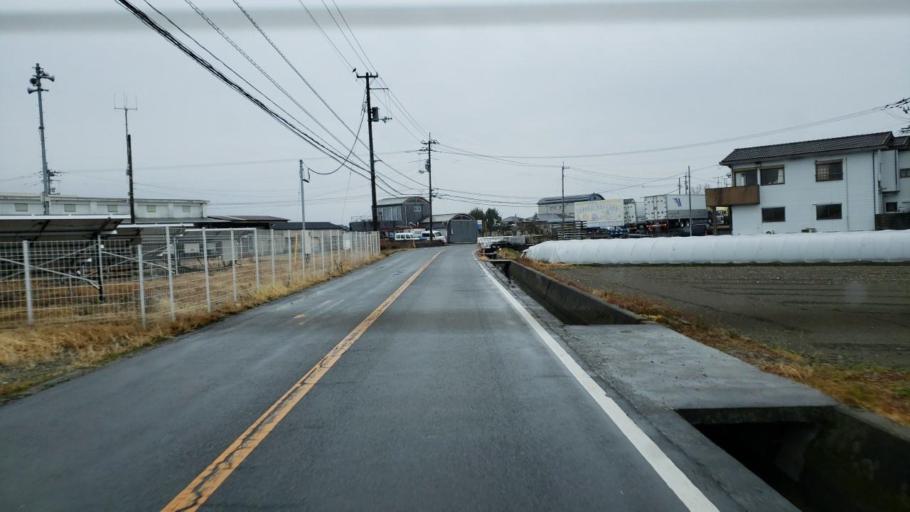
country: JP
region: Tokushima
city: Ishii
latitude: 34.1014
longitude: 134.4024
